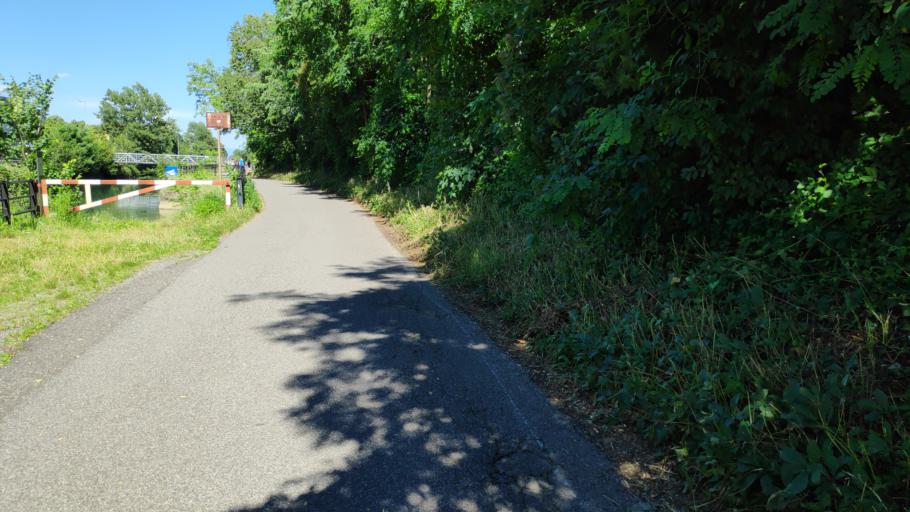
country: IT
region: Lombardy
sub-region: Citta metropolitana di Milano
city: Gorgonzola
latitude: 45.5337
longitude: 9.4160
